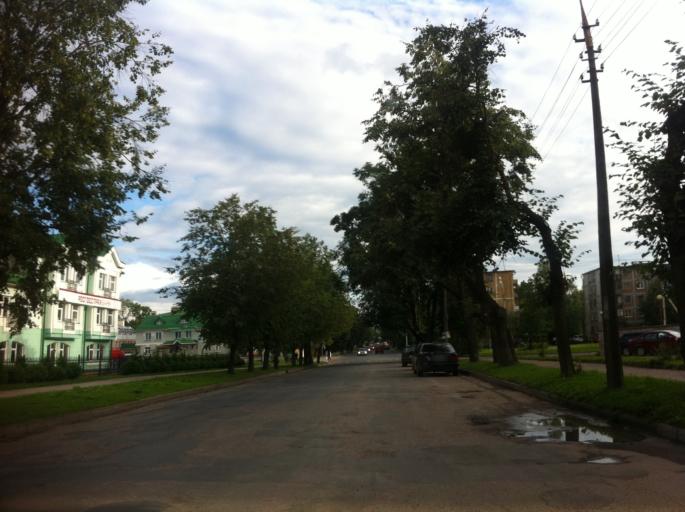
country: RU
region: Pskov
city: Pskov
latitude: 57.8226
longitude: 28.3198
